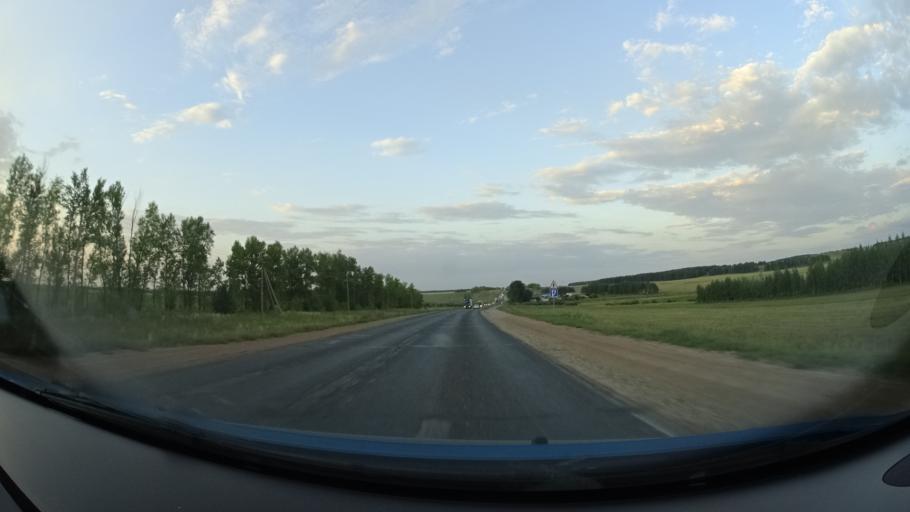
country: RU
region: Orenburg
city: Severnoye
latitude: 54.2113
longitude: 52.7066
